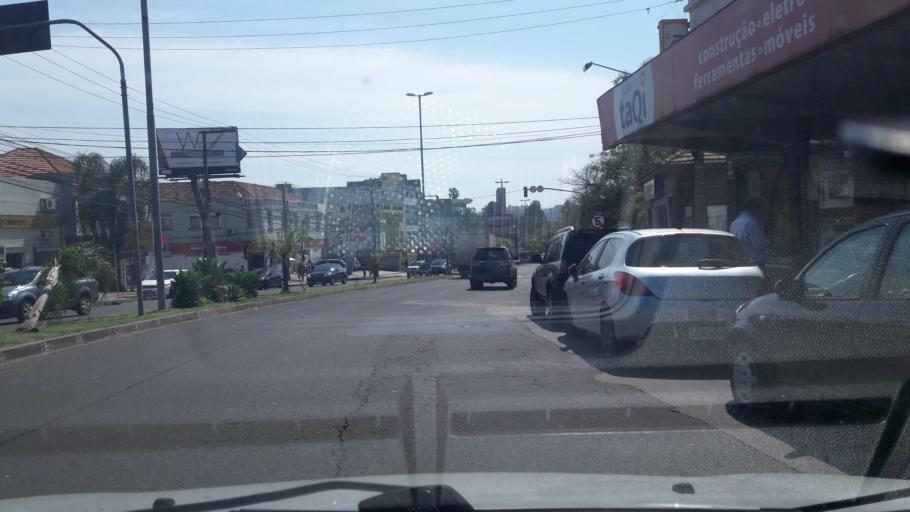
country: BR
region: Rio Grande do Sul
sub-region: Guaiba
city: Guaiba
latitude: -30.1133
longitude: -51.2551
